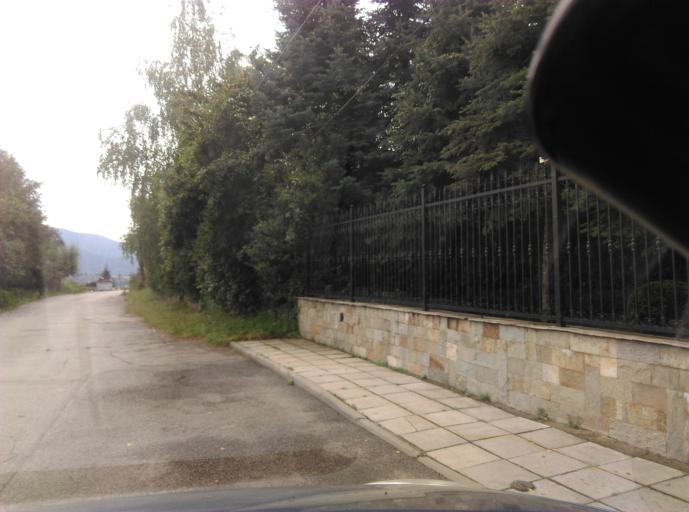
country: BG
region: Sofia-Capital
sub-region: Stolichna Obshtina
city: Sofia
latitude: 42.6024
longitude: 23.3985
